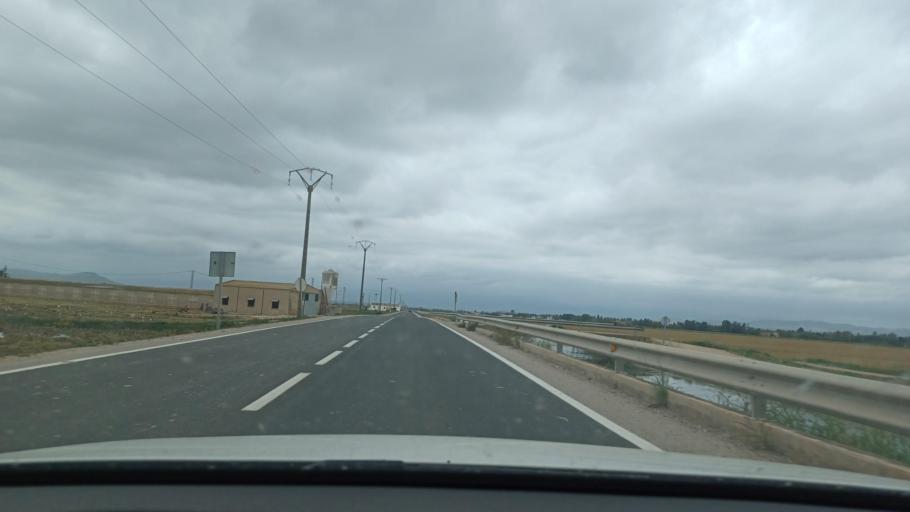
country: ES
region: Catalonia
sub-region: Provincia de Tarragona
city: Deltebre
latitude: 40.7065
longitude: 0.7022
